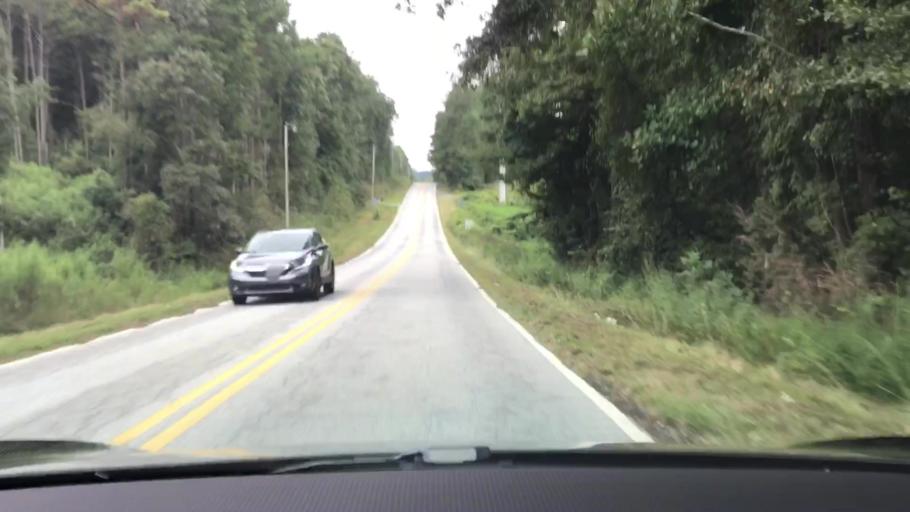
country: US
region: Georgia
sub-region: Barrow County
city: Auburn
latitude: 34.0510
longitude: -83.8179
